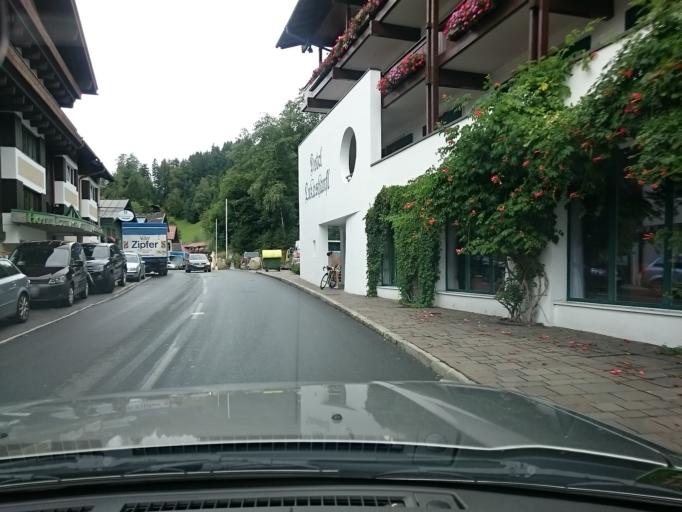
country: AT
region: Salzburg
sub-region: Politischer Bezirk Zell am See
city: Bruck an der Grossglocknerstrasse
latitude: 47.2875
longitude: 12.8245
